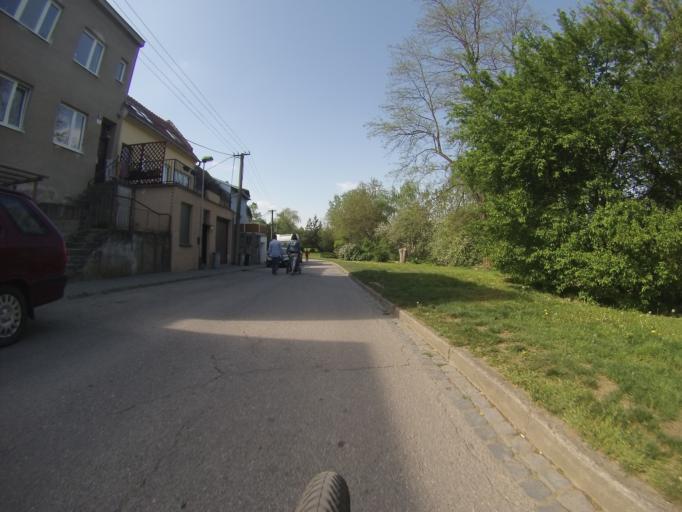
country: CZ
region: South Moravian
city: Troubsko
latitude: 49.2225
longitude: 16.5344
